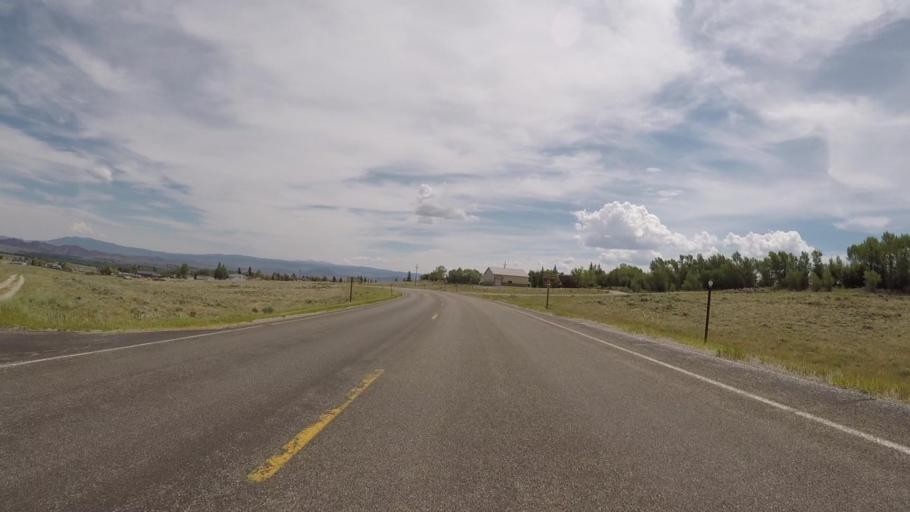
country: US
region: Wyoming
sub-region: Carbon County
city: Saratoga
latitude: 41.2035
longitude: -106.8029
